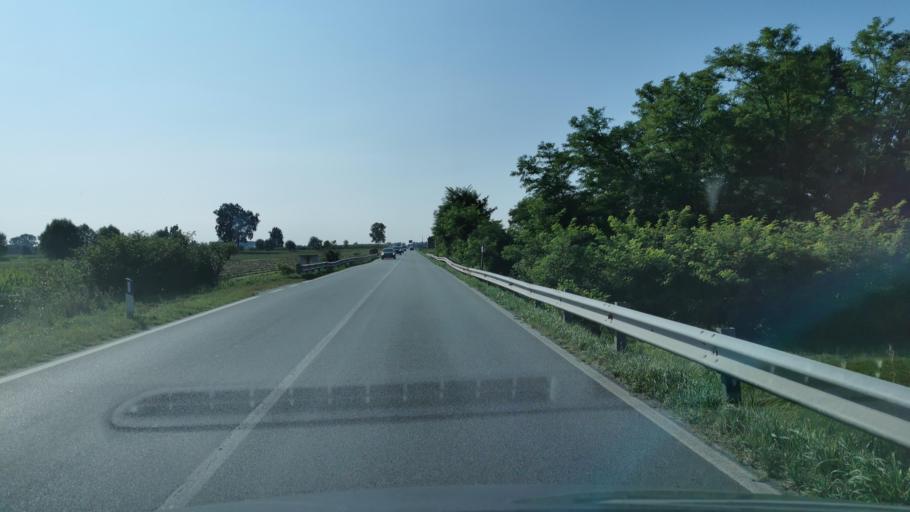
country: IT
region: Piedmont
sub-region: Provincia di Cuneo
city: Carde
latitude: 44.7256
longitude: 7.4337
